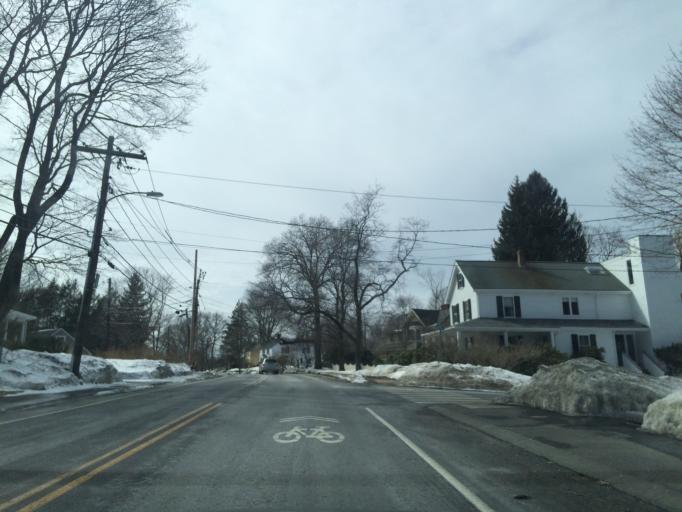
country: US
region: Massachusetts
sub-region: Middlesex County
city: Lexington
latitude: 42.4477
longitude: -71.2437
